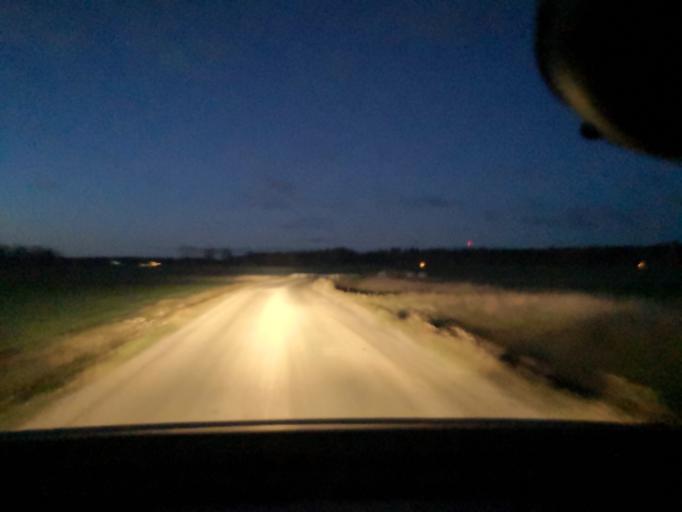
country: SE
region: Uppsala
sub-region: Heby Kommun
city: Heby
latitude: 59.9260
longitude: 16.7547
